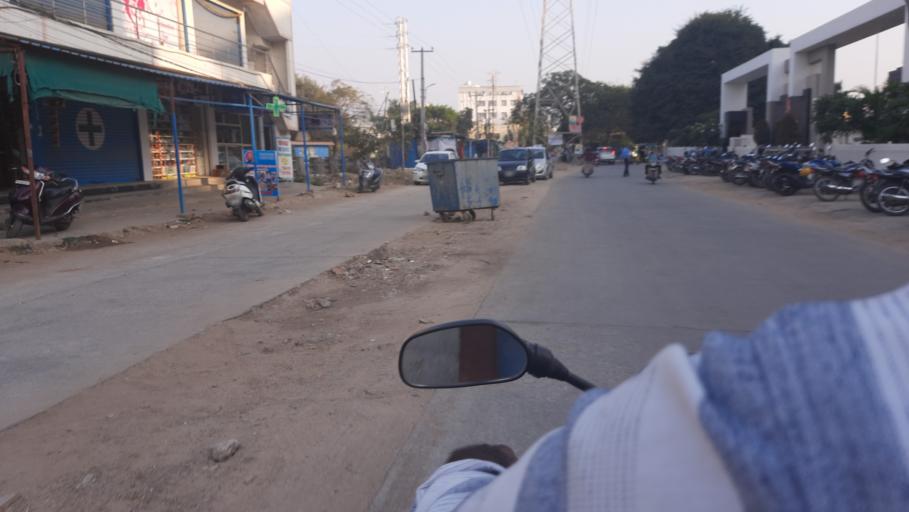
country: IN
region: Telangana
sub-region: Rangareddi
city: Secunderabad
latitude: 17.4971
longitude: 78.5428
